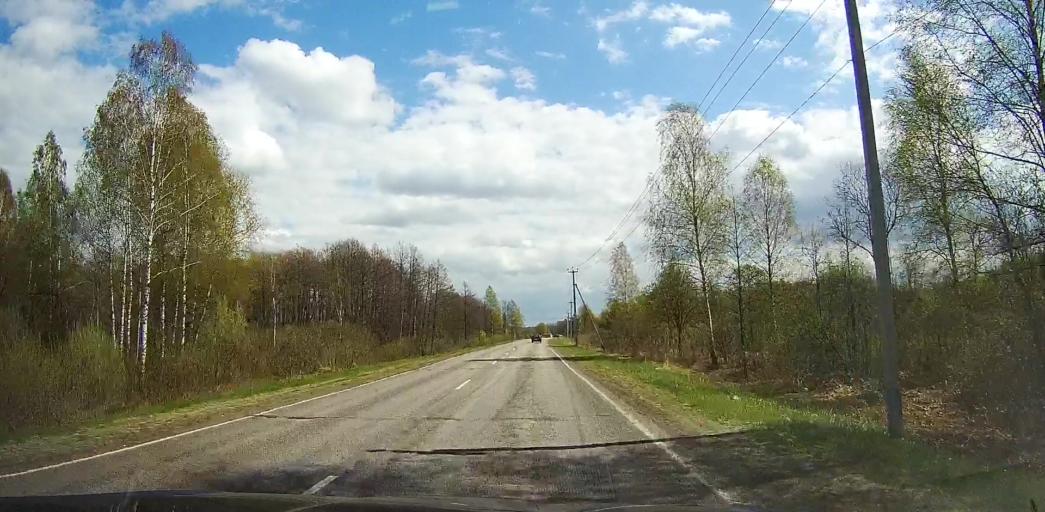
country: RU
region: Moskovskaya
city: Davydovo
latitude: 55.5504
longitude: 38.7989
